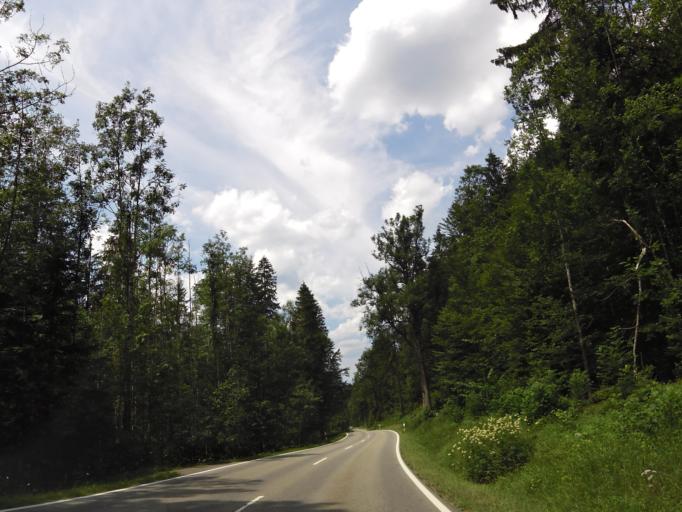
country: DE
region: Bavaria
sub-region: Upper Bavaria
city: Reit im Winkl
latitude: 47.6636
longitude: 12.5082
